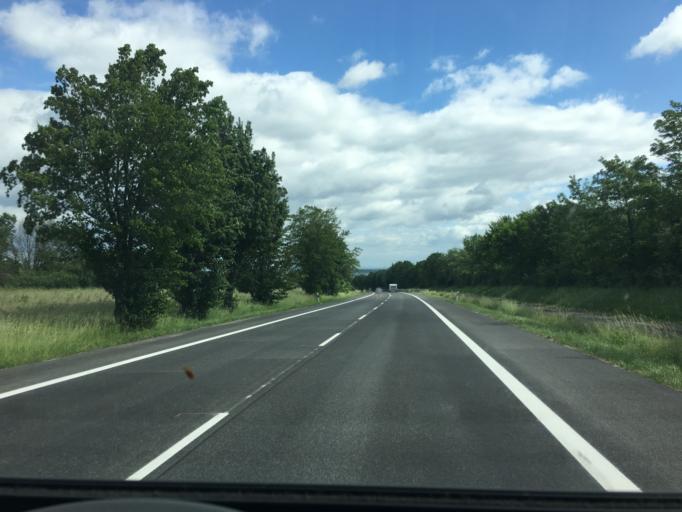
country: DE
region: Rheinland-Pfalz
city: Kalenborn
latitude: 50.5702
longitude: 7.0262
